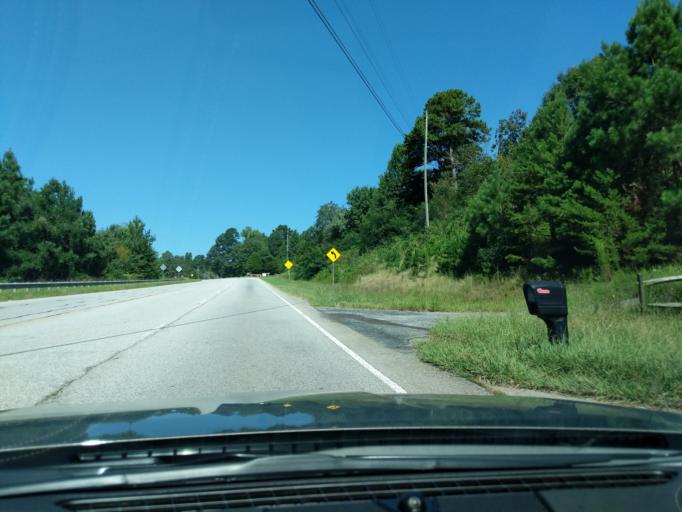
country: US
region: Georgia
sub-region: Habersham County
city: Demorest
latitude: 34.5760
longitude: -83.5958
